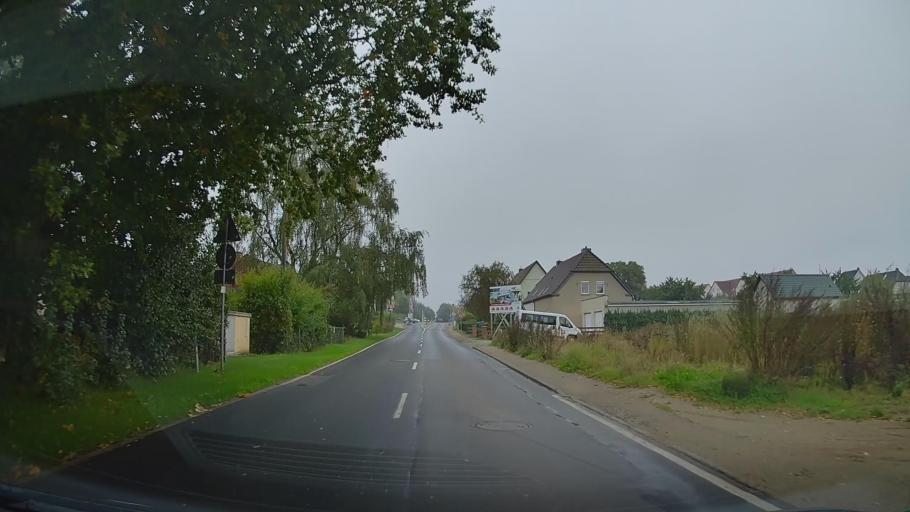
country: DE
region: Mecklenburg-Vorpommern
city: Wismar
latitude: 53.9053
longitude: 11.4050
